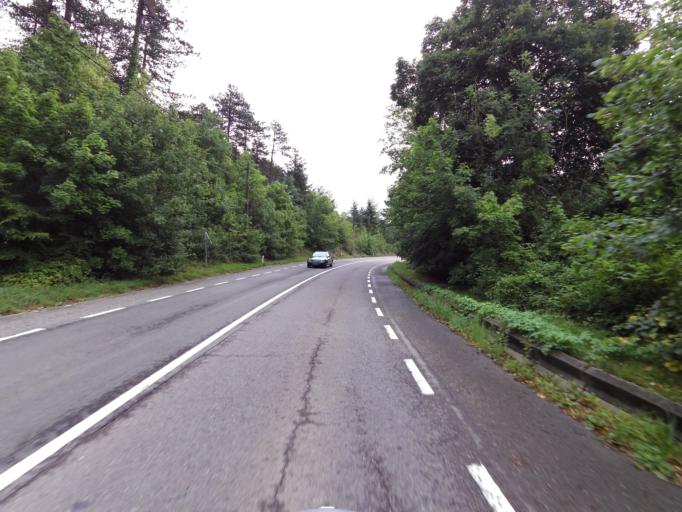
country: BE
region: Wallonia
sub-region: Province de Namur
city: Rochefort
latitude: 50.1350
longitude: 5.1859
